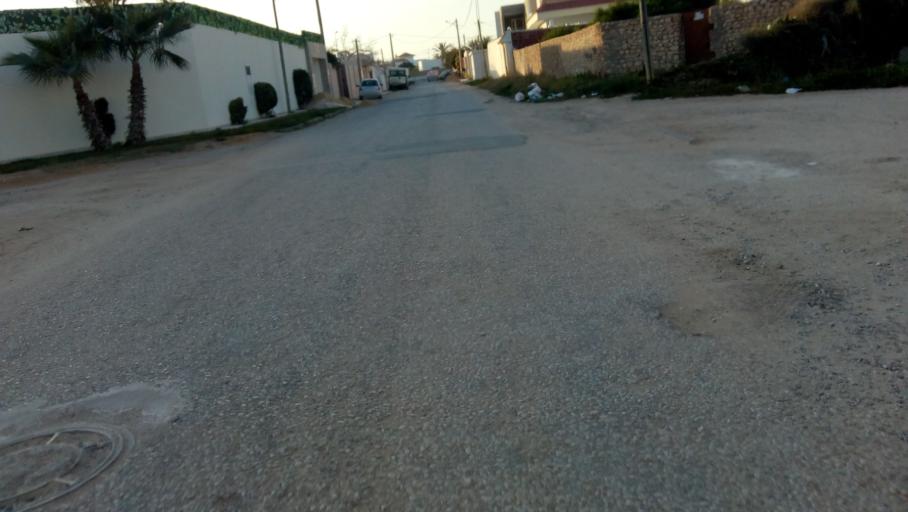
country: TN
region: Safaqis
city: Sfax
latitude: 34.7528
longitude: 10.7335
